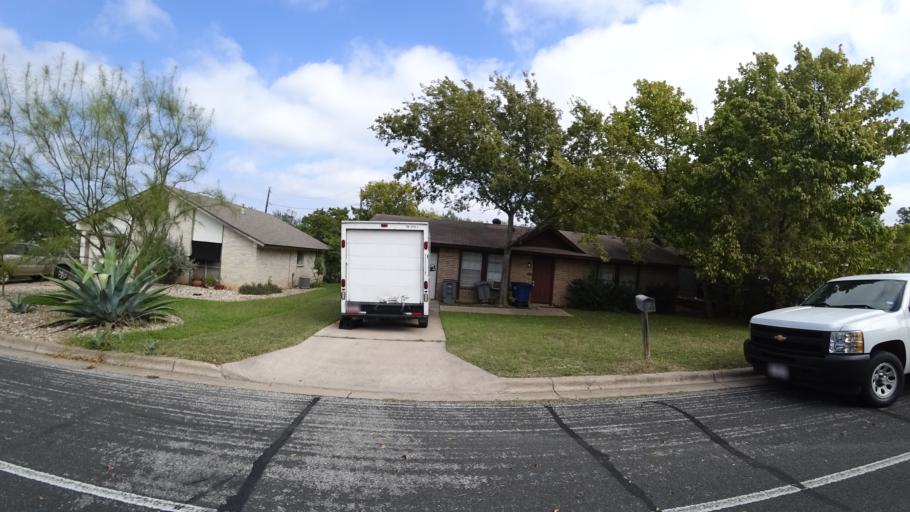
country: US
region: Texas
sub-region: Travis County
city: Shady Hollow
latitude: 30.2007
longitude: -97.8373
